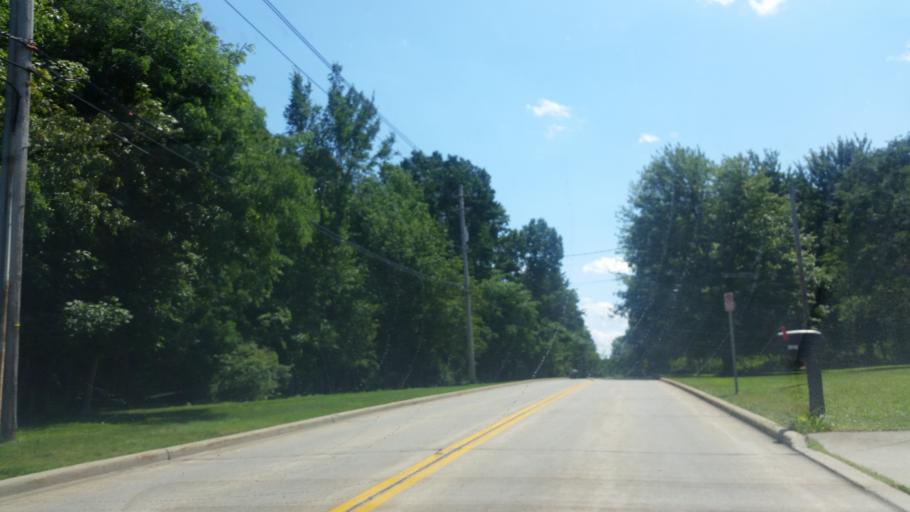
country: US
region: Ohio
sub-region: Cuyahoga County
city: Orange
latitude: 41.4539
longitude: -81.4634
